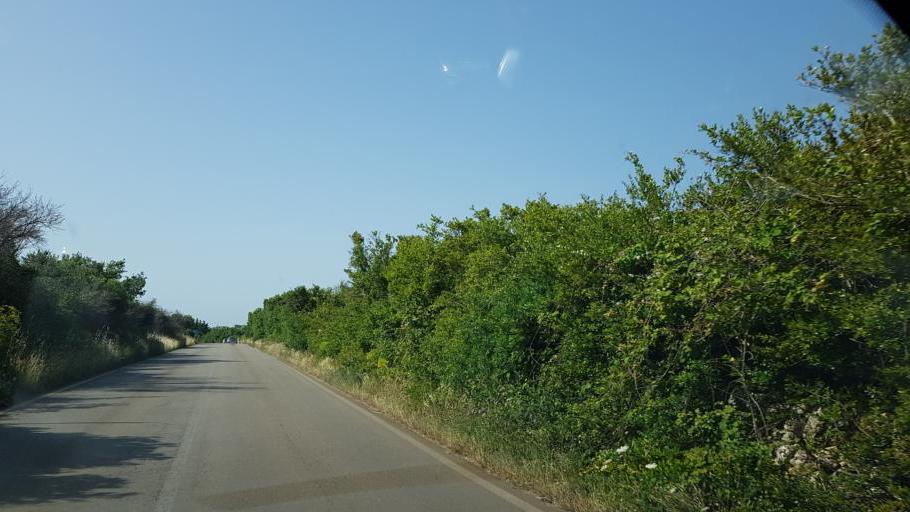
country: IT
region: Apulia
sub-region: Provincia di Lecce
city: Porto Cesareo
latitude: 40.3278
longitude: 17.8531
